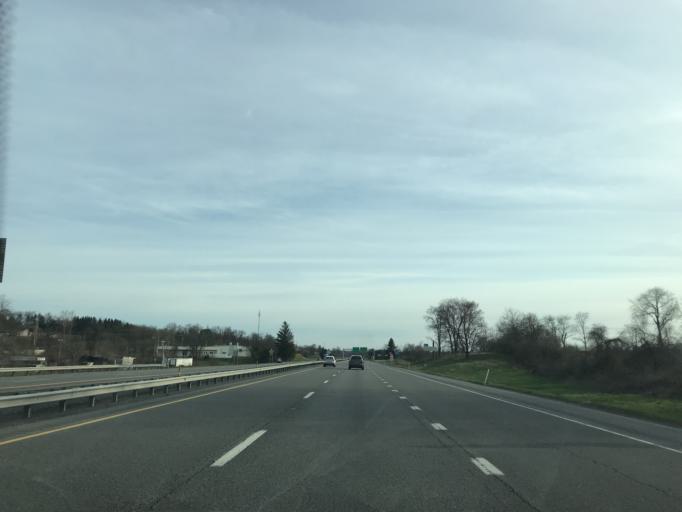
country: US
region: Pennsylvania
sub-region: Union County
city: New Columbia
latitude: 41.0577
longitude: -76.8371
